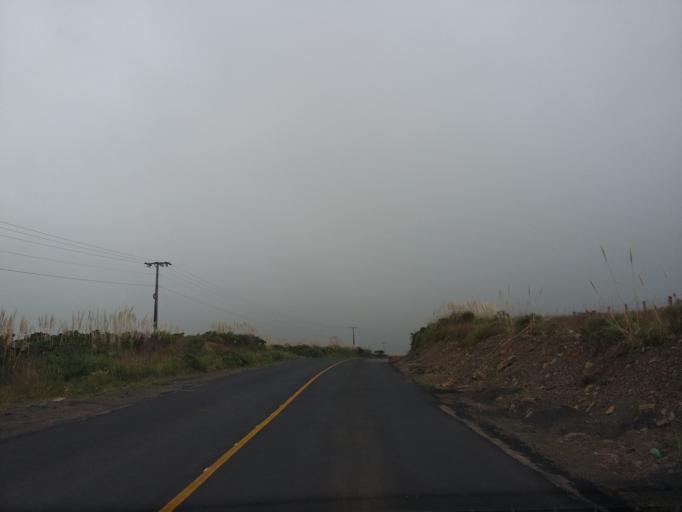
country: BR
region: Santa Catarina
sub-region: Lauro Muller
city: Lauro Muller
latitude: -28.3876
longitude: -49.5534
